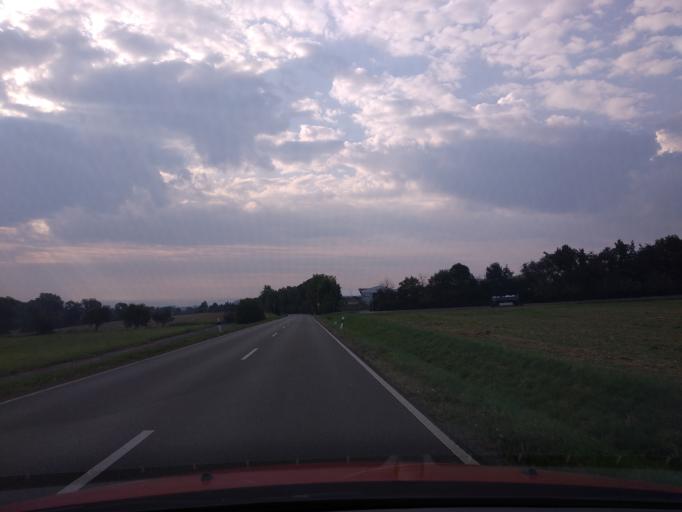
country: DE
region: Hesse
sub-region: Regierungsbezirk Kassel
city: Calden
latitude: 51.3735
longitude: 9.3850
